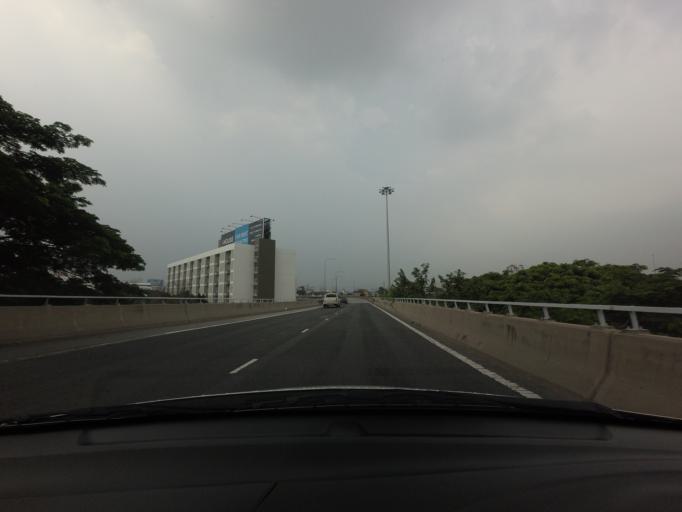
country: TH
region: Bangkok
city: Watthana
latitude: 13.7507
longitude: 100.5915
